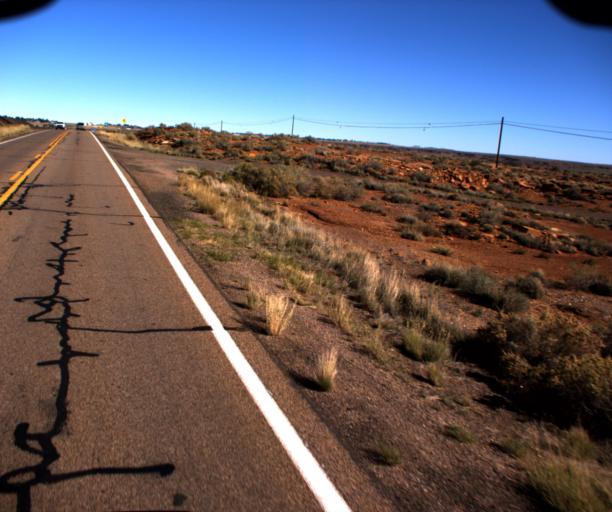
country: US
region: Arizona
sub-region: Navajo County
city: Holbrook
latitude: 34.8823
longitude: -110.1626
